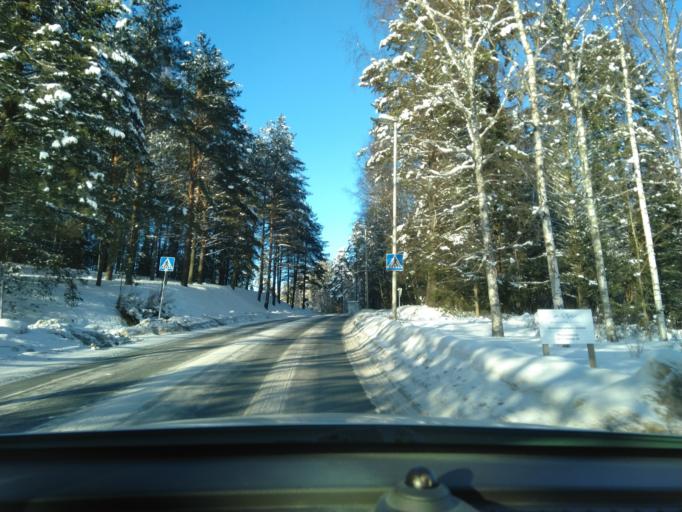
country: FI
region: Haeme
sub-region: Haemeenlinna
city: Haemeenlinna
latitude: 60.9876
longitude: 24.4175
